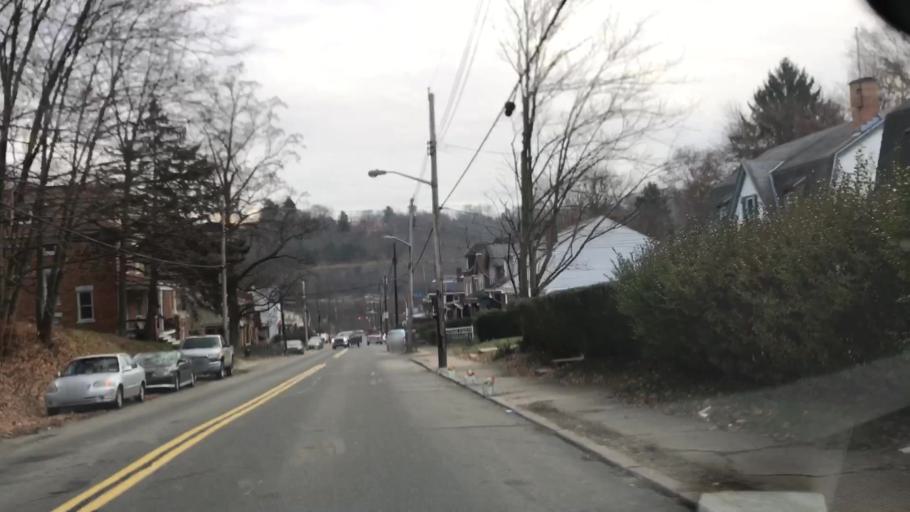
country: US
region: Pennsylvania
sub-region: Allegheny County
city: Millvale
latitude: 40.4888
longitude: -80.0141
